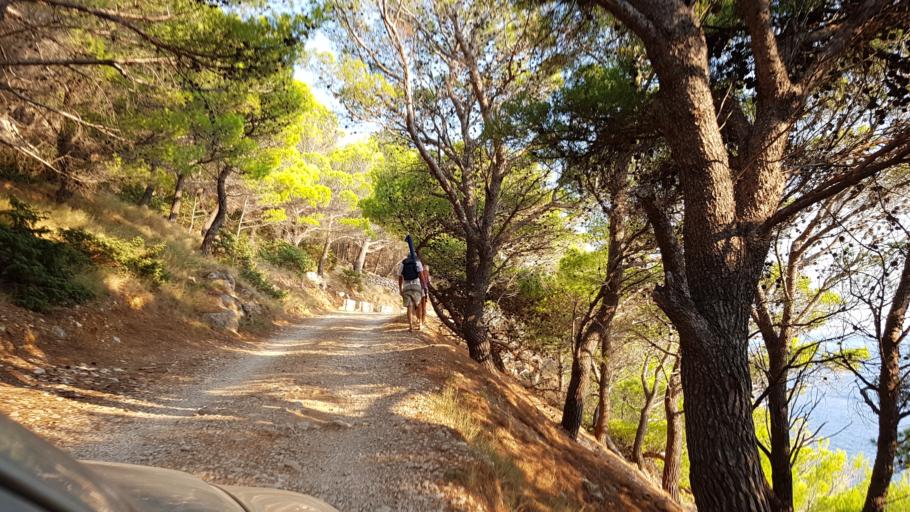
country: HR
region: Splitsko-Dalmatinska
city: Donja Brela
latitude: 43.3890
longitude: 16.8971
